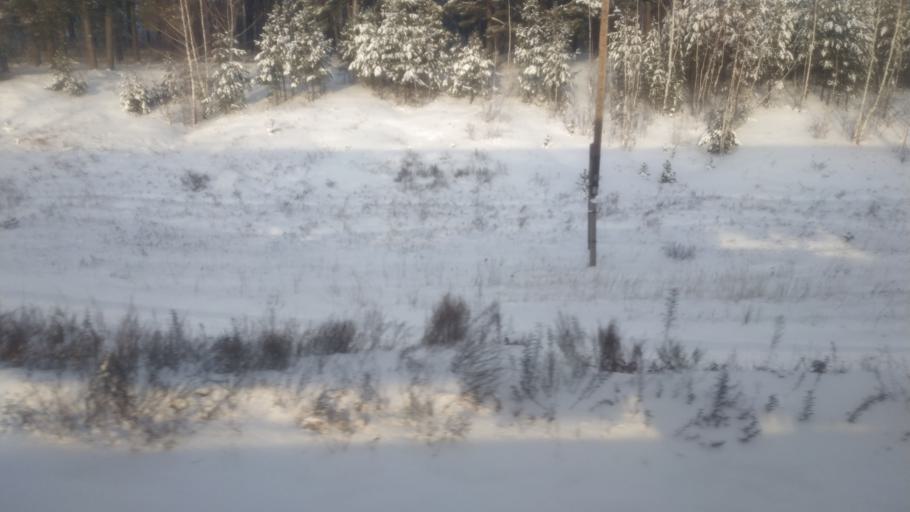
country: RU
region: Kirov
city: Krasnaya Polyana
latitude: 56.2462
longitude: 51.1669
